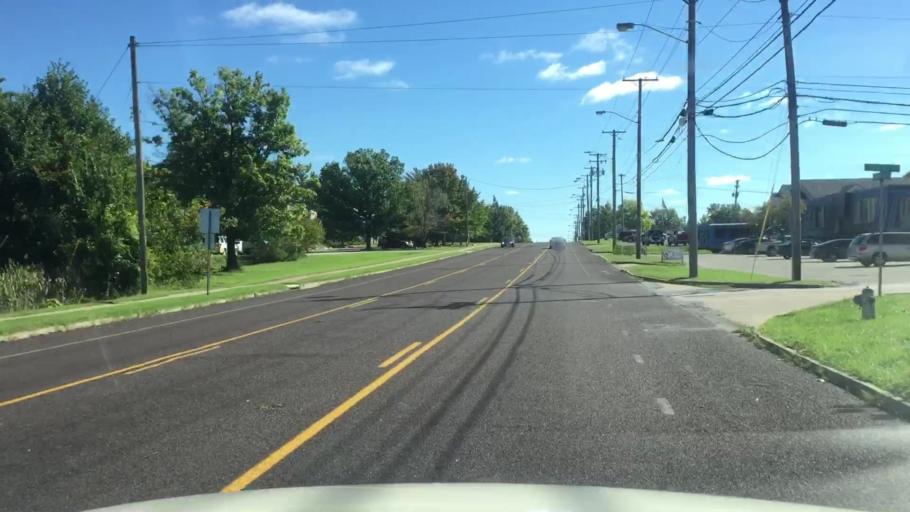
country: US
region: Missouri
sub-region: Boone County
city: Columbia
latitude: 38.9676
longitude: -92.3622
